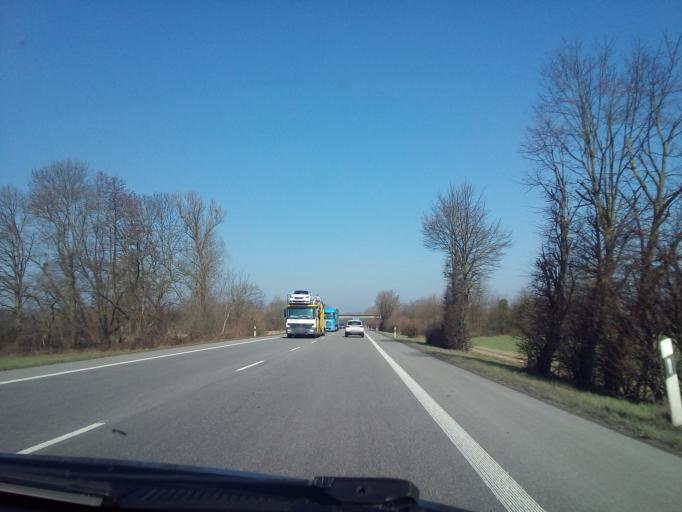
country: DE
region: Baden-Wuerttemberg
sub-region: Karlsruhe Region
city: Iffezheim
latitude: 48.8120
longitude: 8.1352
